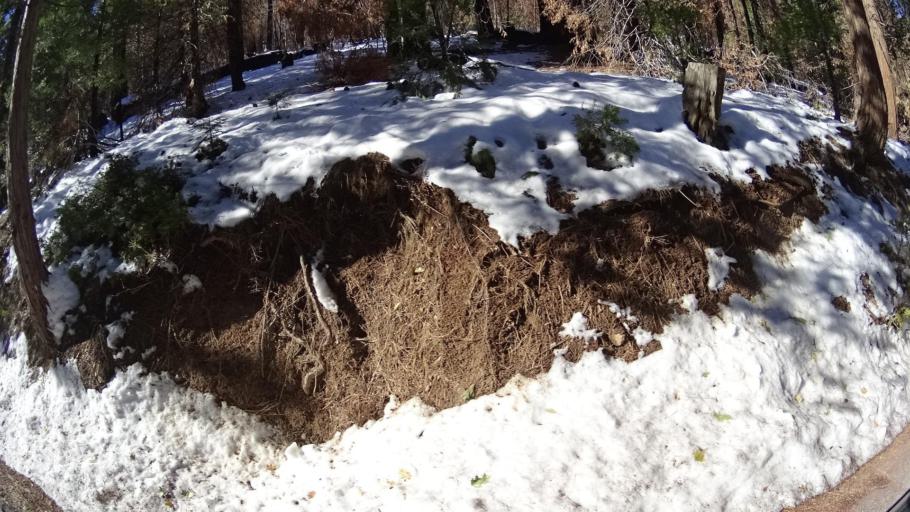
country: US
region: California
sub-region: Kern County
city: Alta Sierra
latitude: 35.7317
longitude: -118.5595
